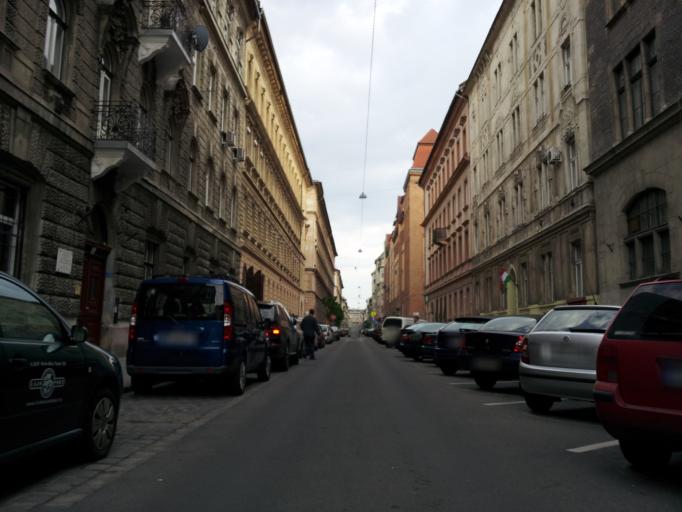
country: HU
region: Budapest
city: Budapest VII. keruelet
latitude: 47.5072
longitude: 19.0802
